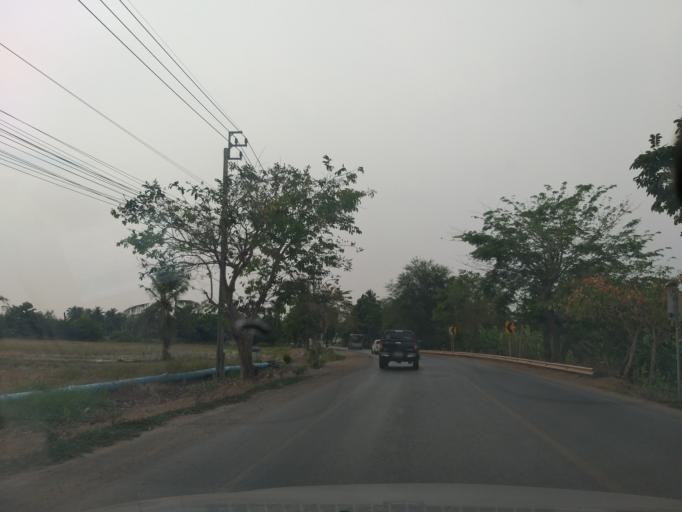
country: TH
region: Bangkok
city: Nong Chok
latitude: 13.8410
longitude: 100.9011
